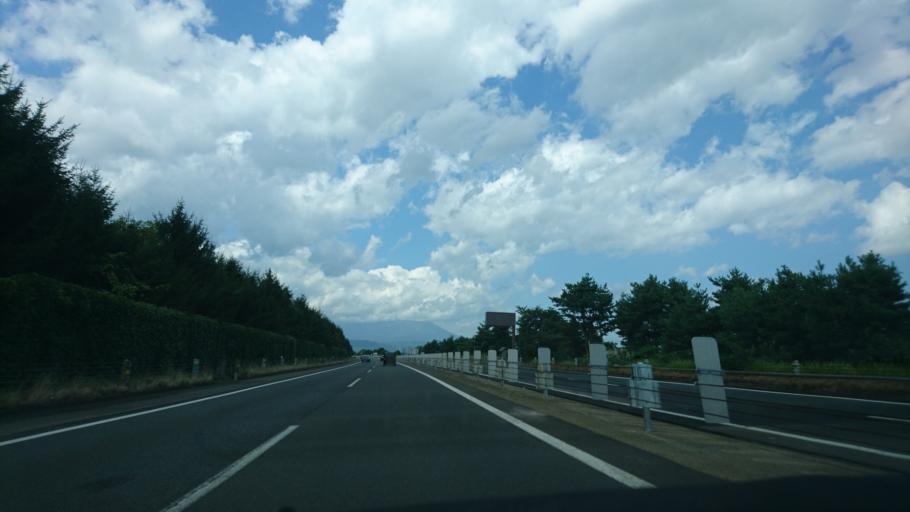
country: JP
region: Iwate
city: Morioka-shi
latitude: 39.6563
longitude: 141.1205
